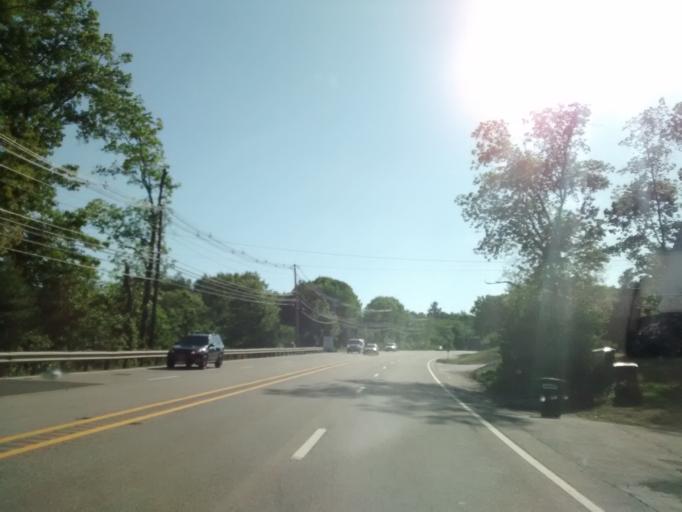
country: US
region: Massachusetts
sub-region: Worcester County
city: Charlton
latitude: 42.1391
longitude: -72.0185
